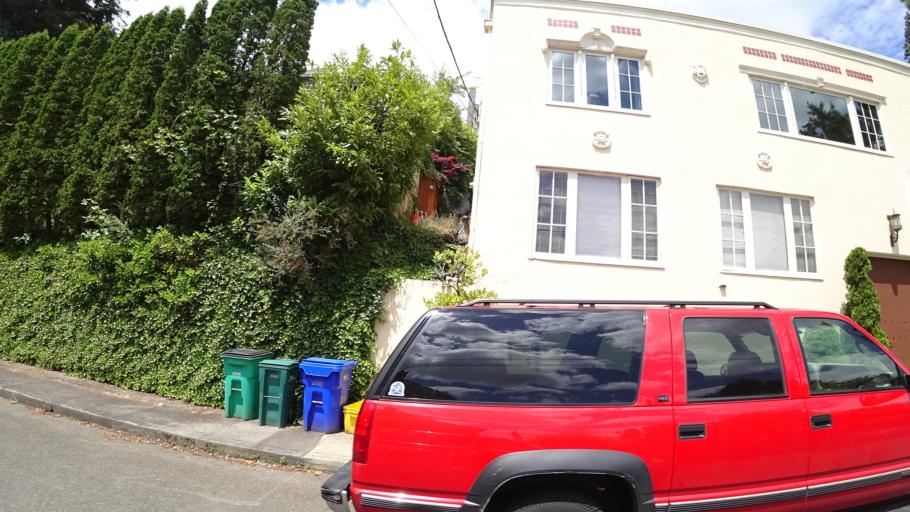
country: US
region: Oregon
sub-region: Multnomah County
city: Portland
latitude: 45.5249
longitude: -122.7037
